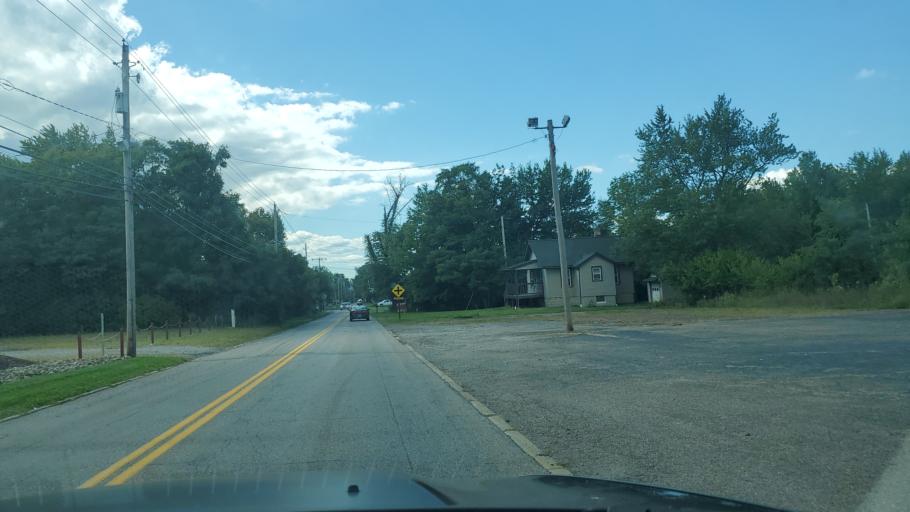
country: US
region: Ohio
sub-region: Mahoning County
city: Boardman
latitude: 40.9879
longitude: -80.6493
